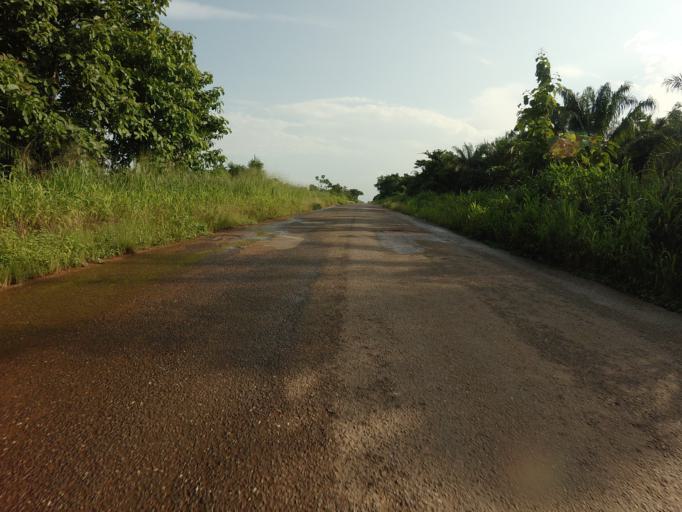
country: GH
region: Volta
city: Hohoe
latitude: 7.0820
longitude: 0.4426
